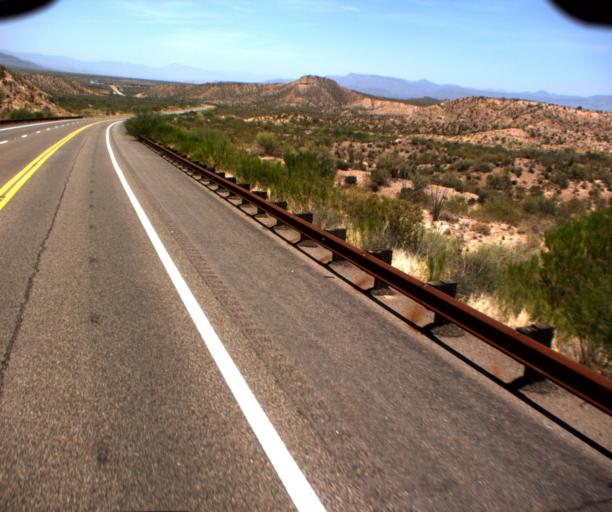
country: US
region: Arizona
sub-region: Gila County
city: Miami
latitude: 33.5854
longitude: -110.9796
